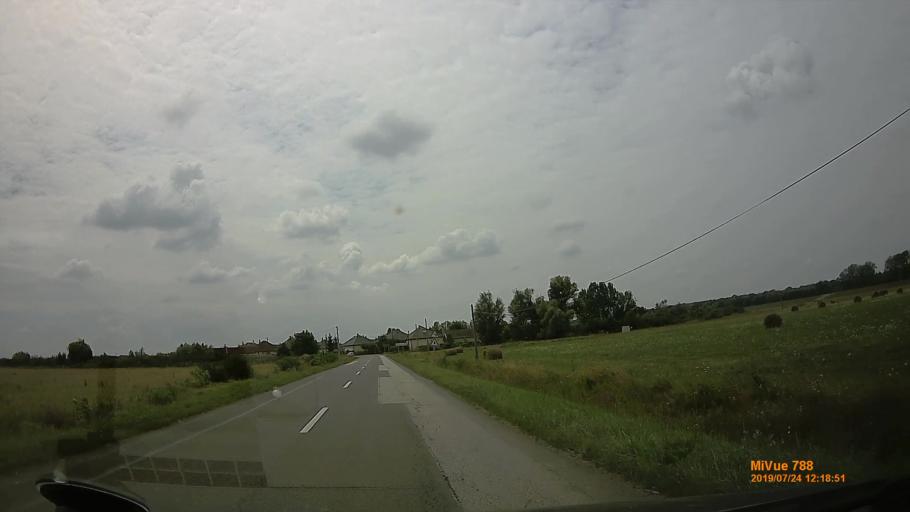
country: HU
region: Szabolcs-Szatmar-Bereg
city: Vasarosnameny
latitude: 48.1460
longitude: 22.3461
